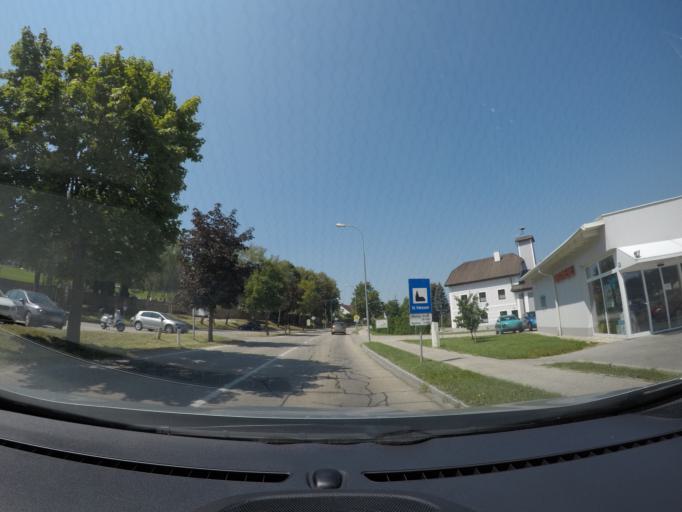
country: AT
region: Lower Austria
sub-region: Politischer Bezirk Sankt Polten
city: Maria-Anzbach
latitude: 48.1890
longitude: 15.9367
